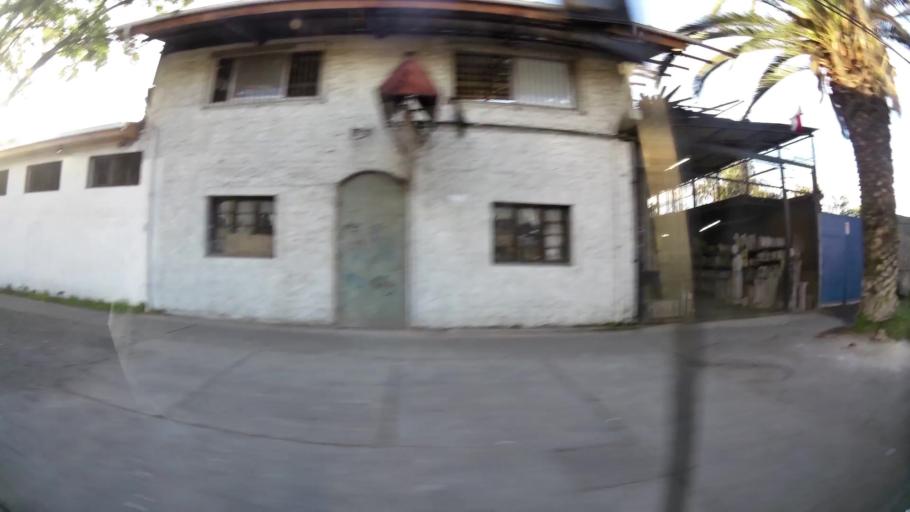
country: CL
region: Santiago Metropolitan
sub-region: Provincia de Santiago
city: Lo Prado
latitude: -33.4449
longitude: -70.6946
